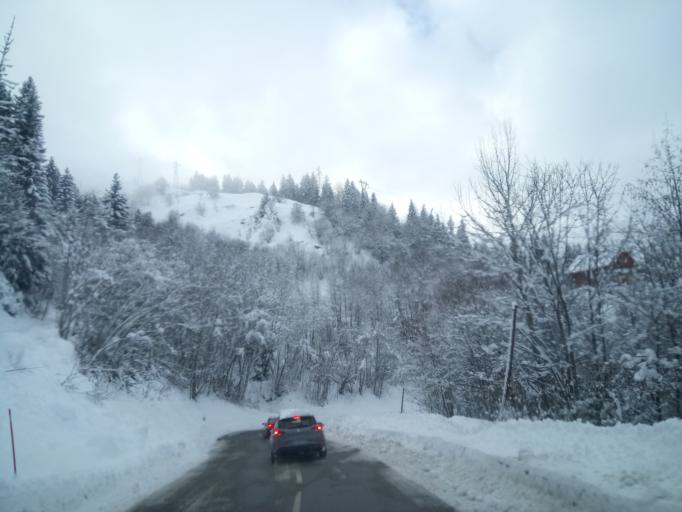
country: FR
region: Rhone-Alpes
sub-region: Departement de la Savoie
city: Saint-Jean-de-Maurienne
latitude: 45.2404
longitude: 6.2801
